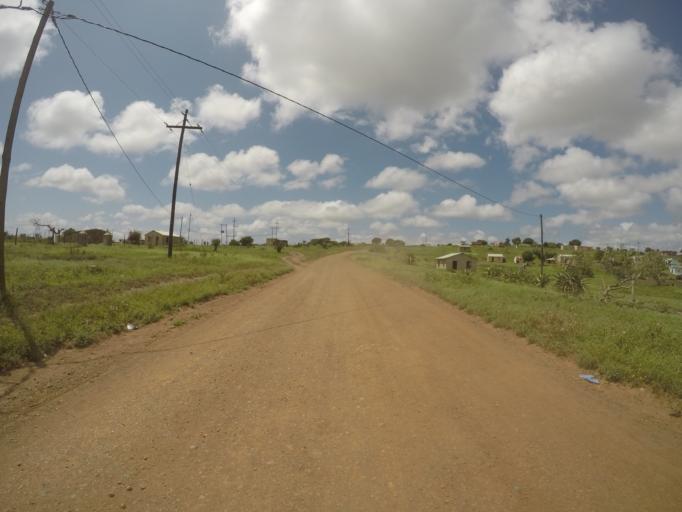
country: ZA
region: KwaZulu-Natal
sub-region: uThungulu District Municipality
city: Empangeni
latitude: -28.5766
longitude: 31.8397
